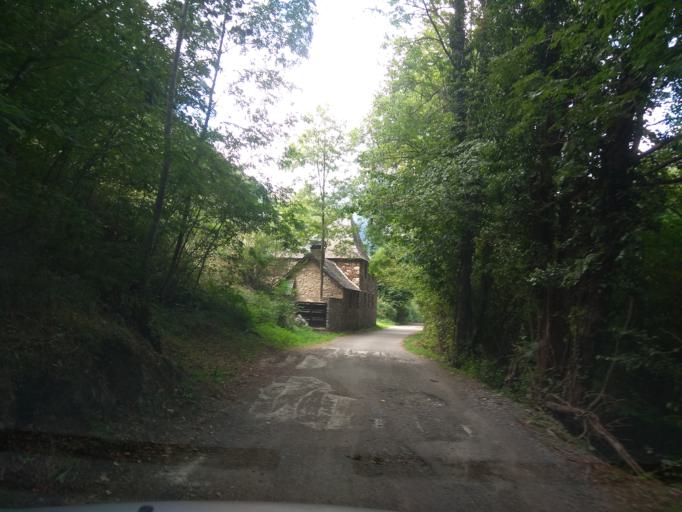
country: ES
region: Catalonia
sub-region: Provincia de Lleida
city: Les
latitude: 42.7578
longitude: 0.6935
